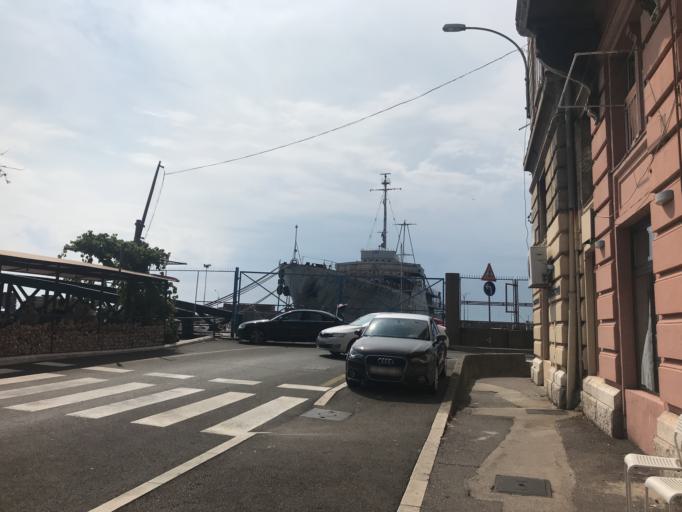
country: HR
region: Primorsko-Goranska
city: Drenova
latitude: 45.3233
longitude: 14.4444
